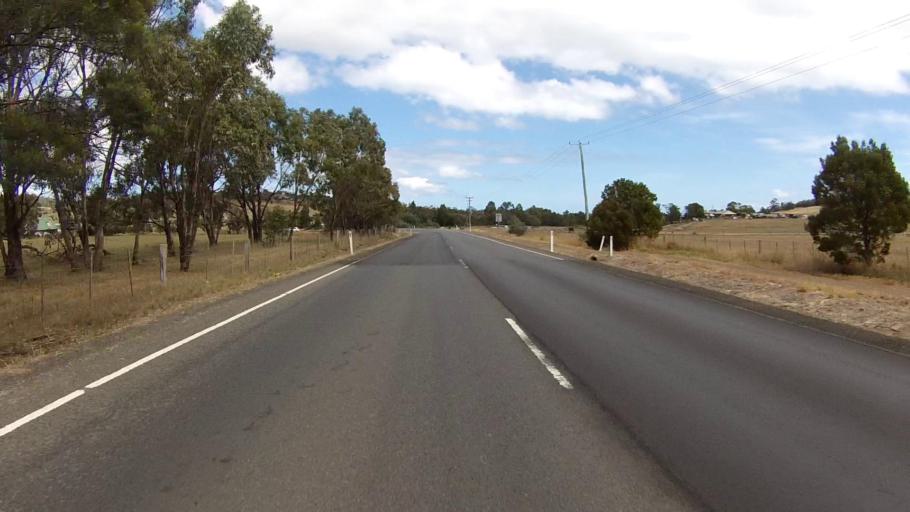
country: AU
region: Tasmania
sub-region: Sorell
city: Sorell
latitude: -42.8291
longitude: 147.6235
